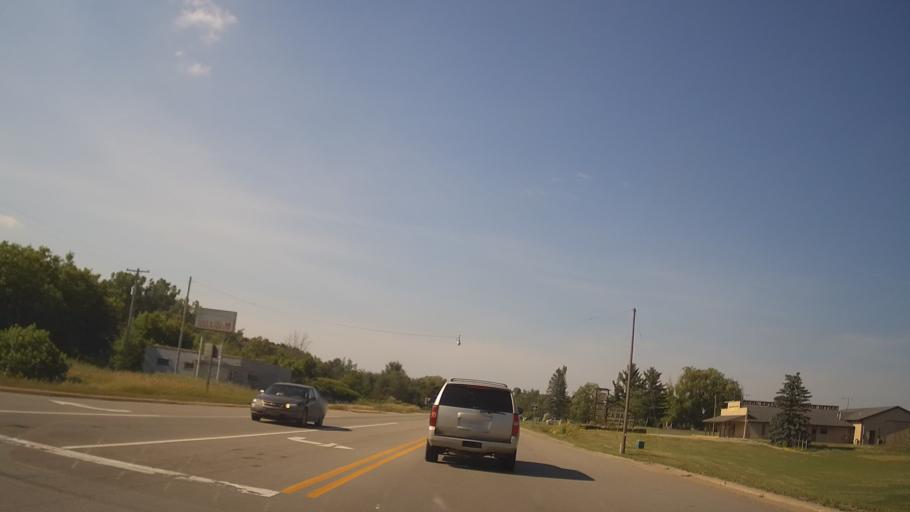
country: US
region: Michigan
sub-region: Ogemaw County
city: West Branch
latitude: 44.2771
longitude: -84.1257
